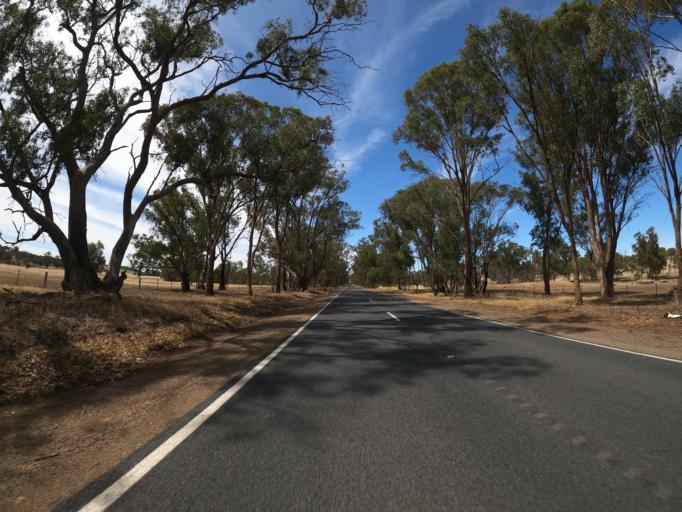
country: AU
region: Victoria
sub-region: Benalla
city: Benalla
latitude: -36.3645
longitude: 145.9694
